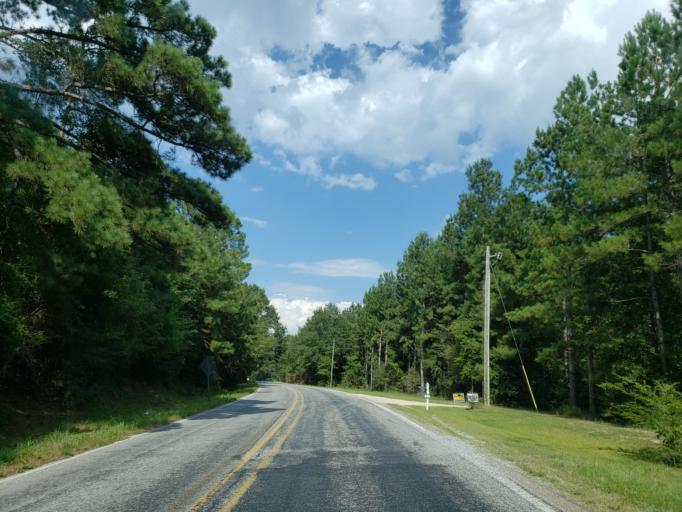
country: US
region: Mississippi
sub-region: Covington County
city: Collins
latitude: 31.6189
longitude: -89.3870
